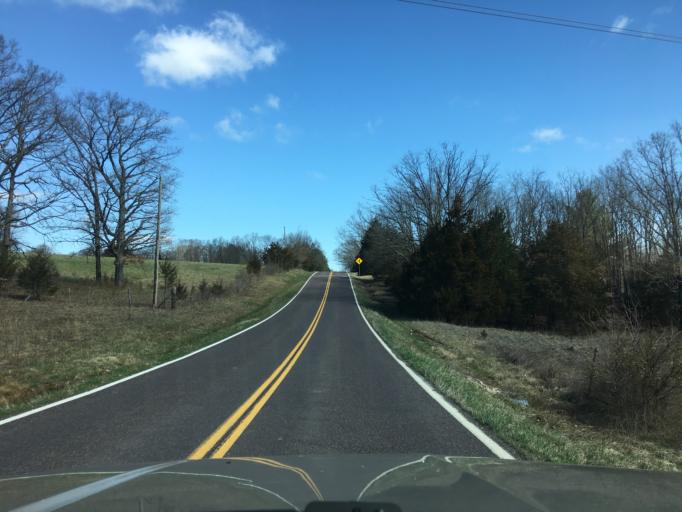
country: US
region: Missouri
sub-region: Franklin County
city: Gerald
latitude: 38.4321
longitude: -91.3344
